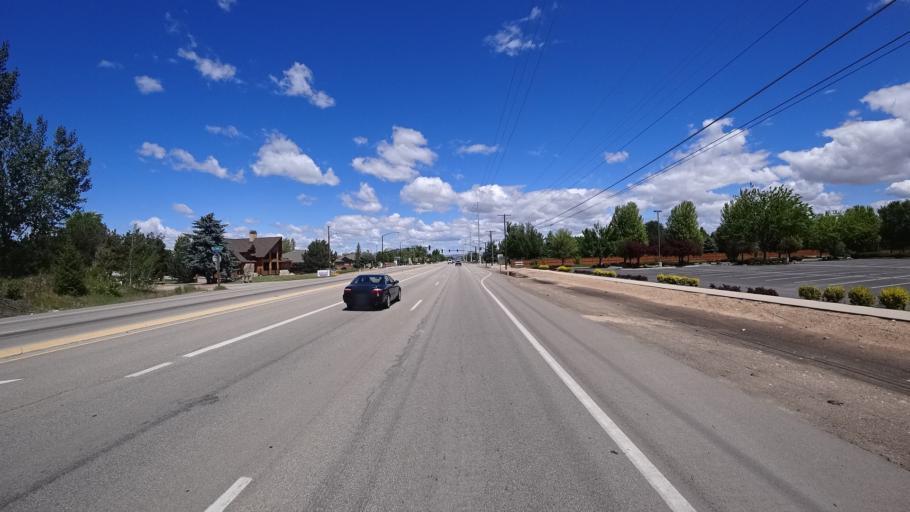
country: US
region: Idaho
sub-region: Ada County
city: Meridian
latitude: 43.6403
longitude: -116.3543
